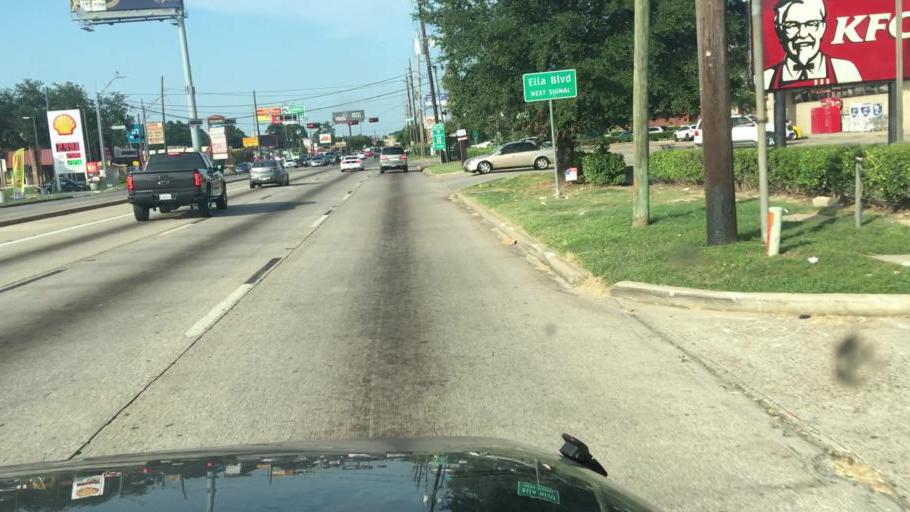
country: US
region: Texas
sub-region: Harris County
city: Spring
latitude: 30.0137
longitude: -95.4515
